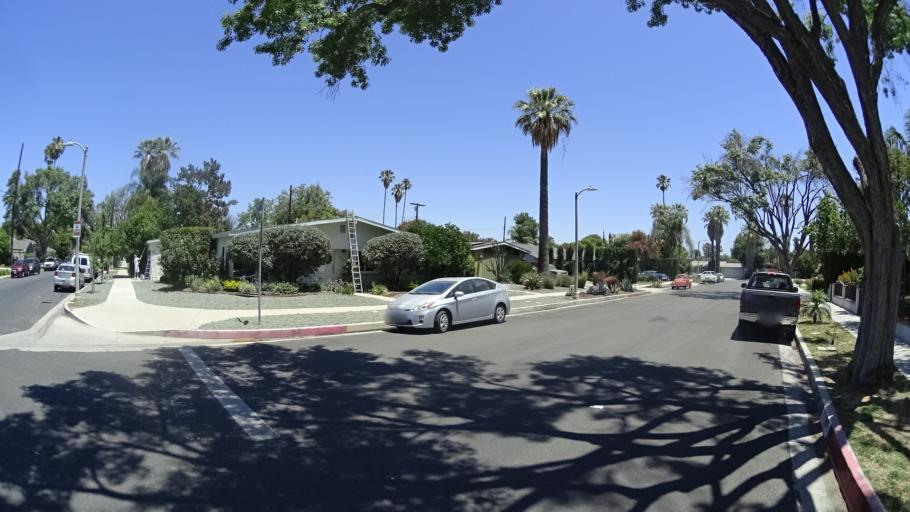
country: US
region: California
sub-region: Los Angeles County
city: Northridge
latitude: 34.1950
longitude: -118.5120
